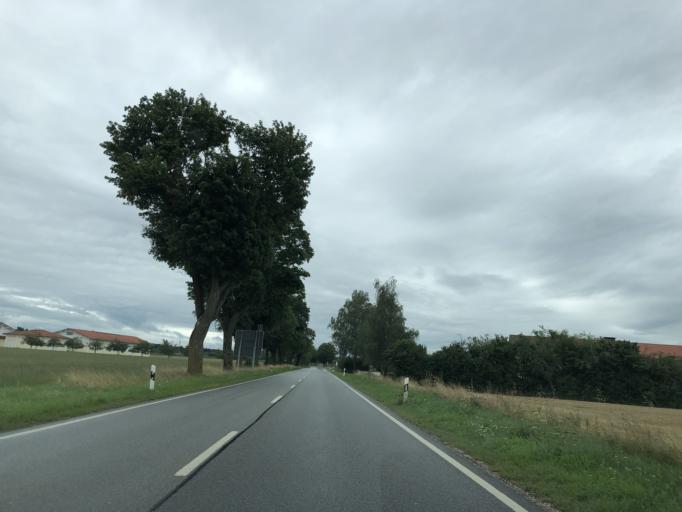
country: DE
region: Bavaria
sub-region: Upper Bavaria
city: Taufkirchen
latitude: 48.0394
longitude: 11.6311
